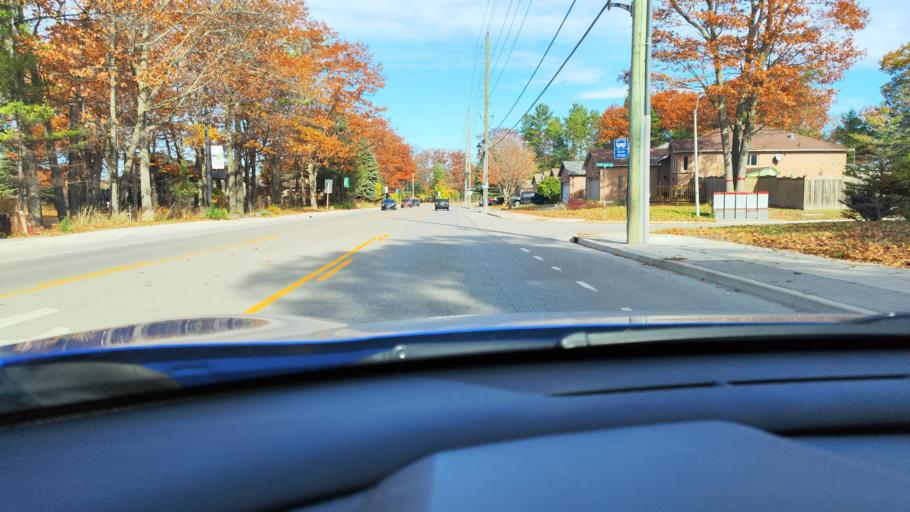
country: CA
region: Ontario
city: Wasaga Beach
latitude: 44.4948
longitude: -80.0430
